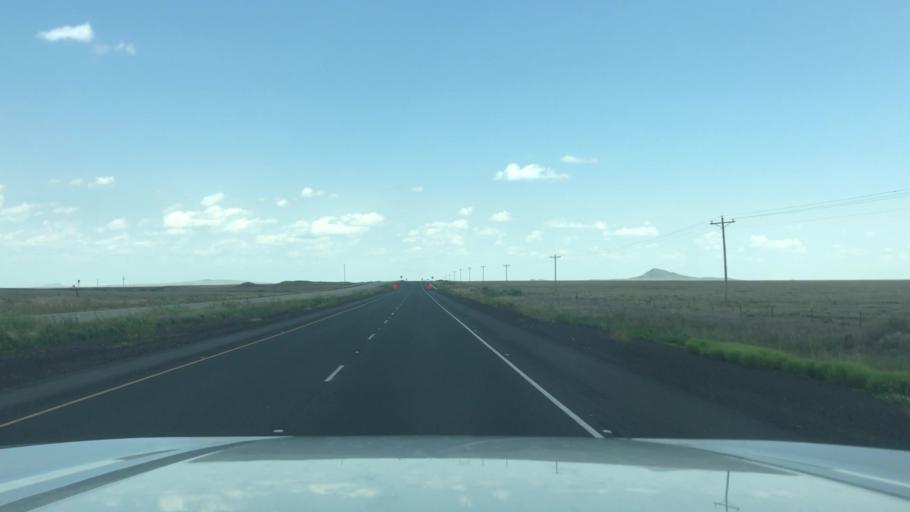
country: US
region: New Mexico
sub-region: Union County
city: Clayton
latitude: 36.6267
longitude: -103.7060
